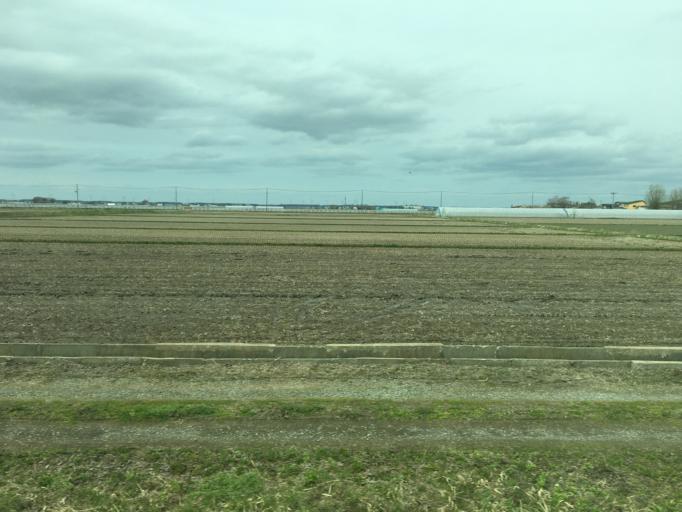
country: JP
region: Aomori
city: Shimokizukuri
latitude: 40.7907
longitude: 140.3698
